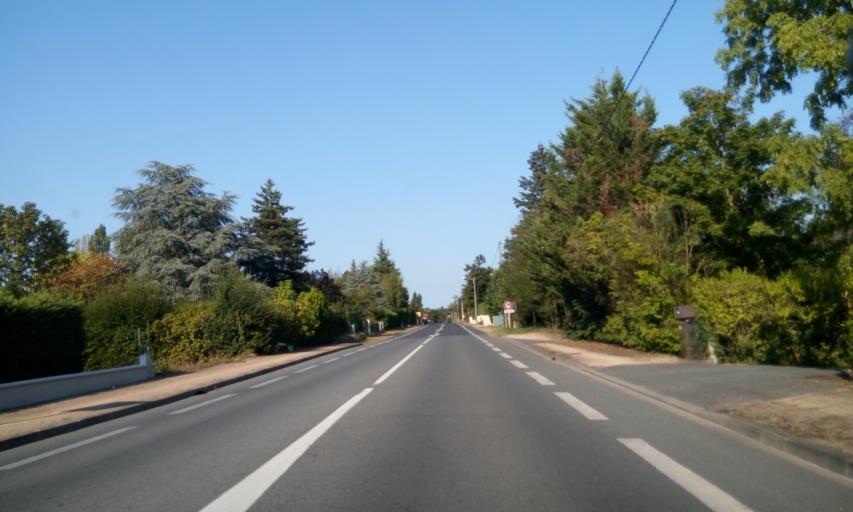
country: FR
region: Rhone-Alpes
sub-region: Departement de l'Ain
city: Trevoux
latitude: 45.9510
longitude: 4.7473
